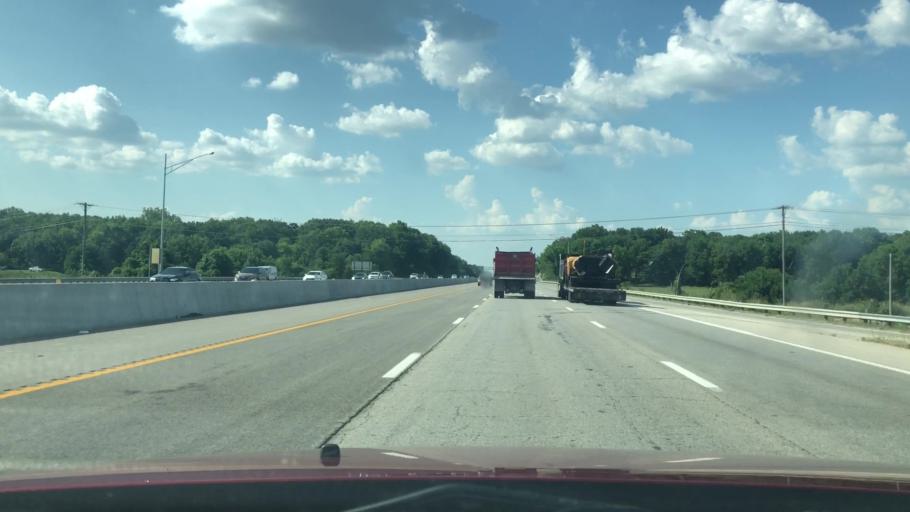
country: US
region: Missouri
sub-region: Christian County
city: Nixa
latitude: 37.1026
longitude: -93.2325
